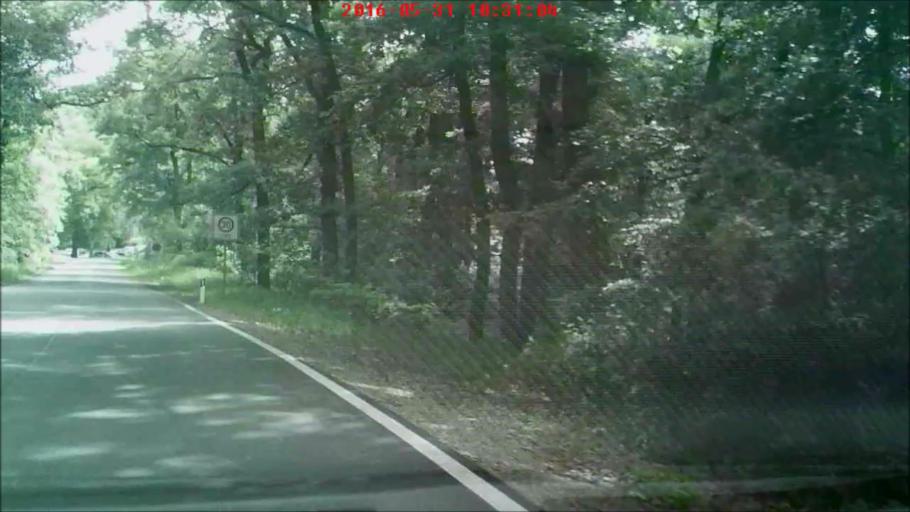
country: DE
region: Saxony-Anhalt
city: Bennungen
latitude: 51.4148
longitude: 11.0964
